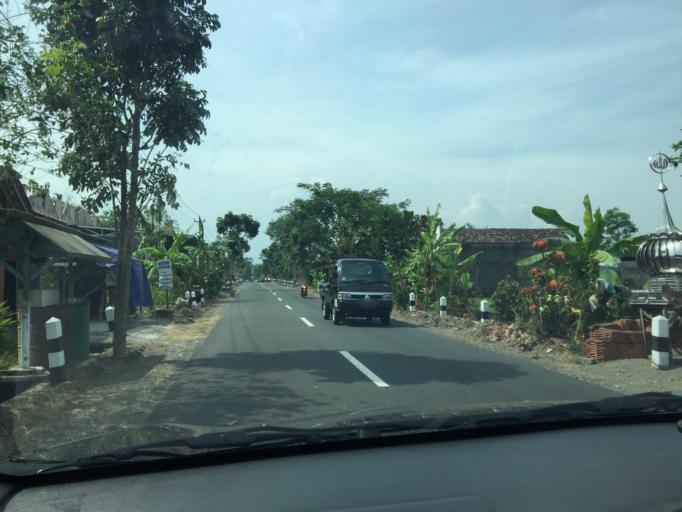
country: ID
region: Central Java
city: Candi Prambanan
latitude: -7.7488
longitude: 110.4812
